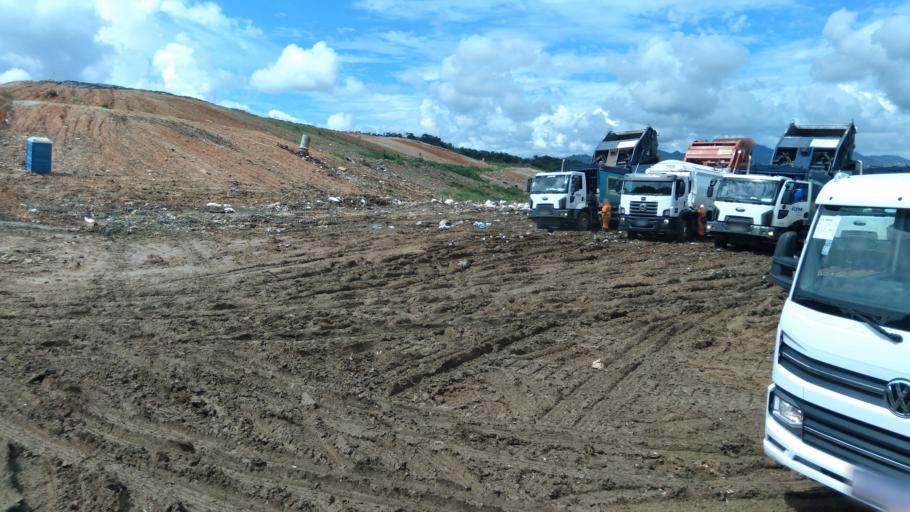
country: BR
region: Minas Gerais
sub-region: Santa Luzia
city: Santa Luzia
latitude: -19.8514
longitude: -43.8461
